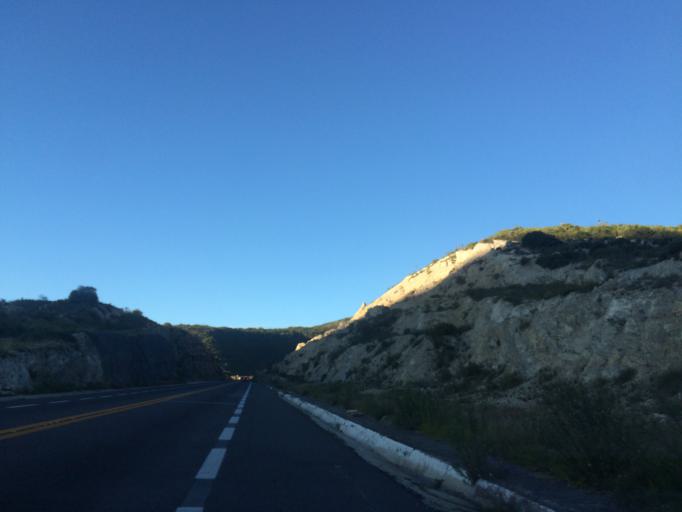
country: MX
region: Puebla
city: Chapuco
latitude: 18.6639
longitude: -97.4565
